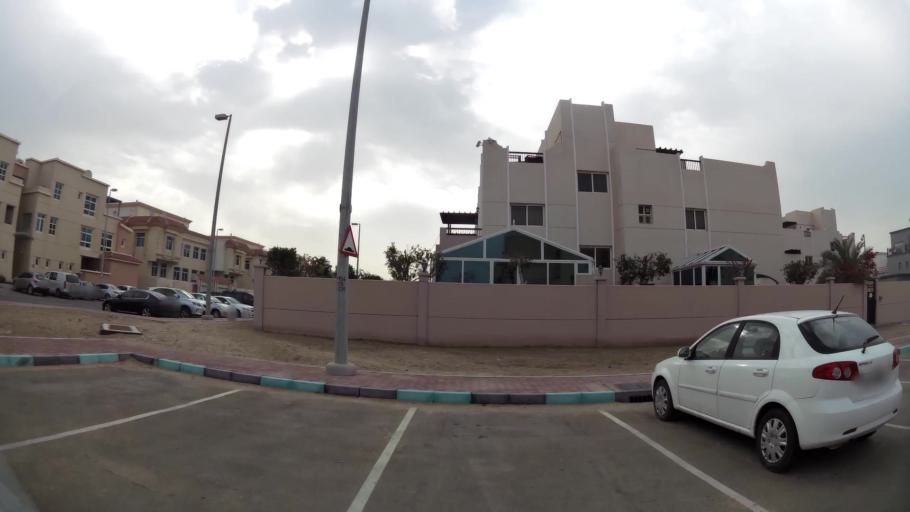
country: AE
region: Abu Dhabi
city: Abu Dhabi
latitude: 24.4729
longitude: 54.3842
